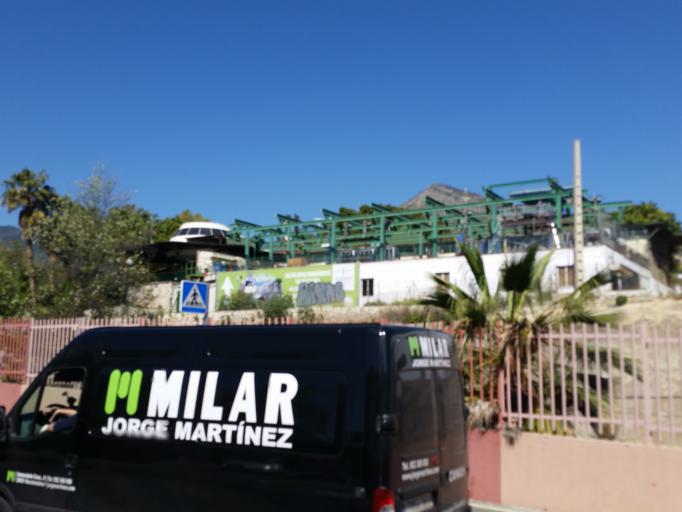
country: ES
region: Andalusia
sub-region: Provincia de Malaga
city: Benalmadena
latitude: 36.5987
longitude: -4.5391
